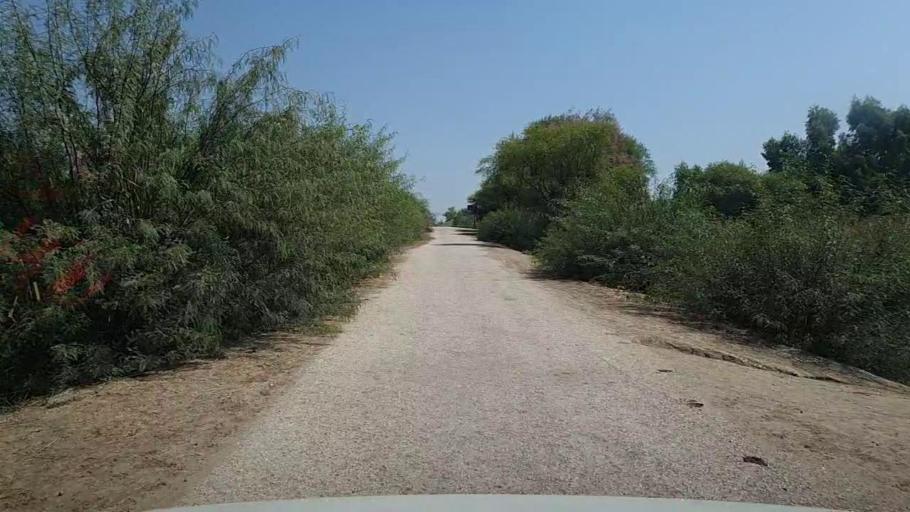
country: PK
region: Sindh
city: Kandhkot
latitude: 28.2886
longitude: 69.3532
